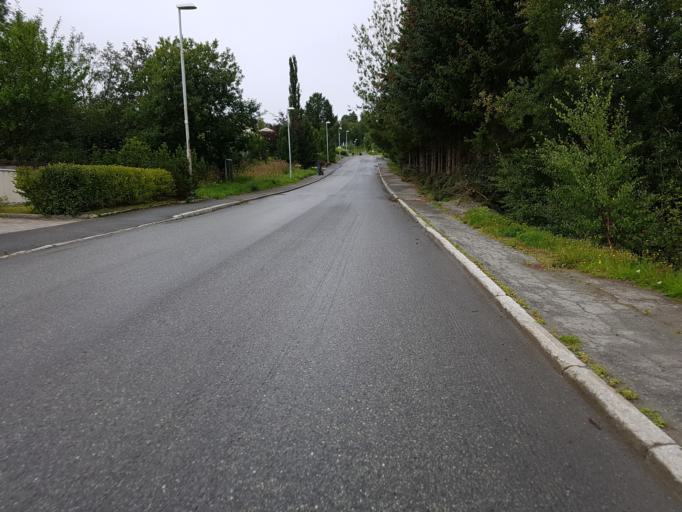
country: NO
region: Sor-Trondelag
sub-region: Trondheim
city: Trondheim
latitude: 63.4018
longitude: 10.3730
